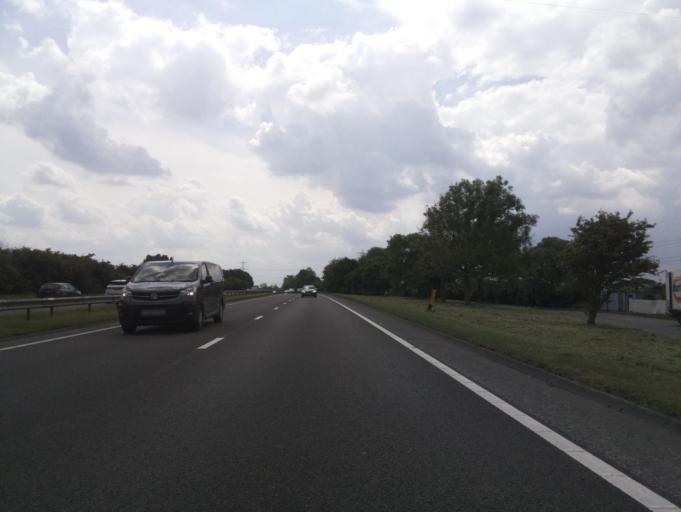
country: GB
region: England
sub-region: North Yorkshire
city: Northallerton
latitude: 54.3545
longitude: -1.3265
